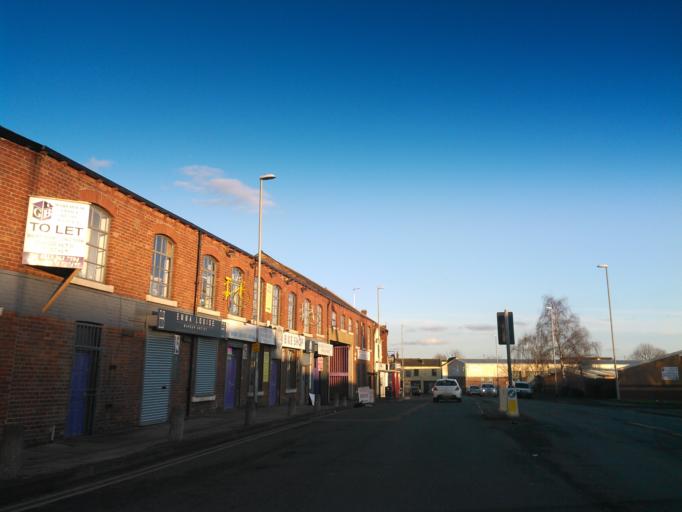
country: GB
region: England
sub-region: City and Borough of Leeds
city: Gildersome
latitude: 53.7935
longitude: -1.5971
